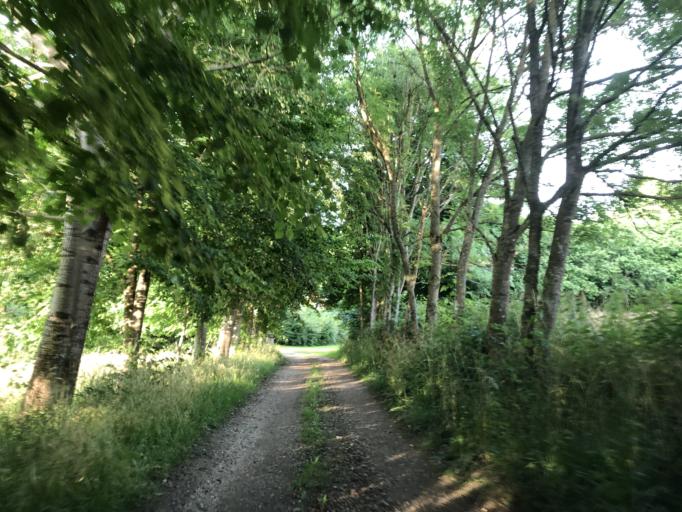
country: DK
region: South Denmark
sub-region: Fredericia Kommune
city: Taulov
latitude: 55.5886
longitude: 9.6150
